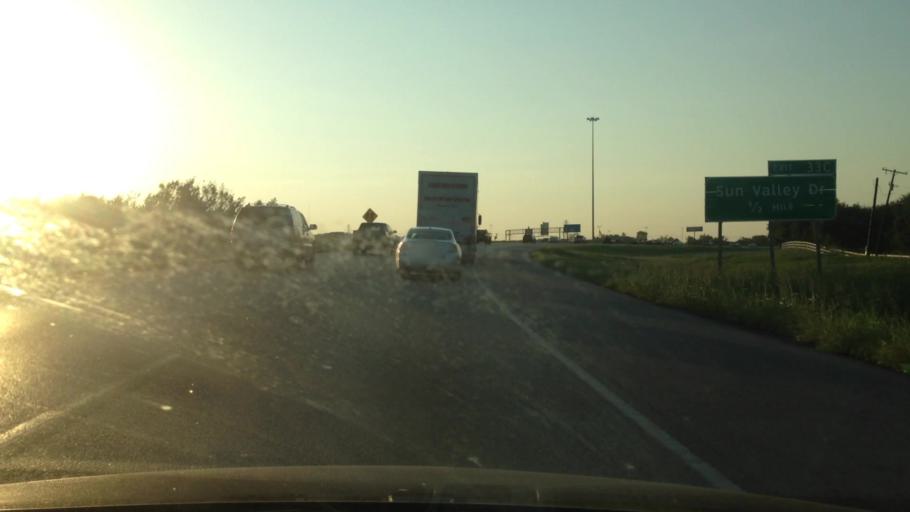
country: US
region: Texas
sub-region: Tarrant County
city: Kennedale
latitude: 32.6700
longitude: -97.2373
